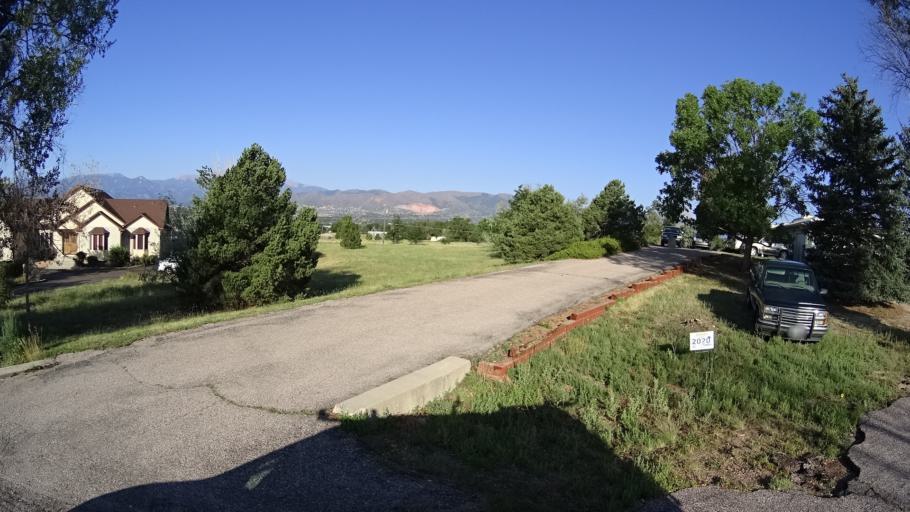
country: US
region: Colorado
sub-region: El Paso County
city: Air Force Academy
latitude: 38.9342
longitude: -104.7820
